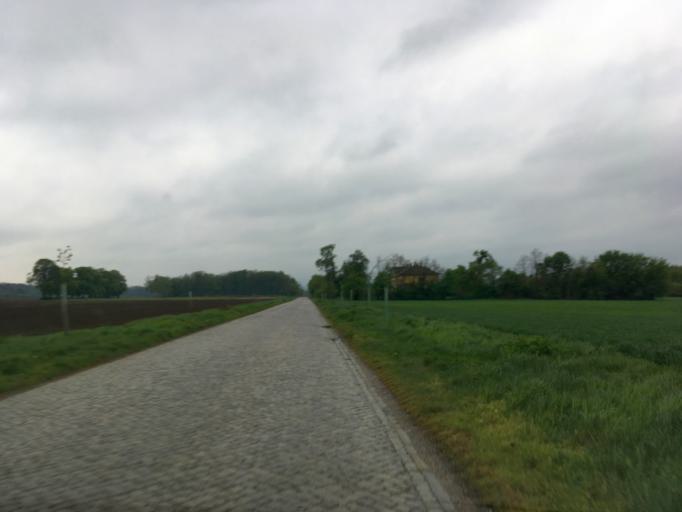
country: AT
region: Lower Austria
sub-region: Politischer Bezirk Bruck an der Leitha
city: Bruck an der Leitha
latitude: 48.0131
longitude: 16.7699
